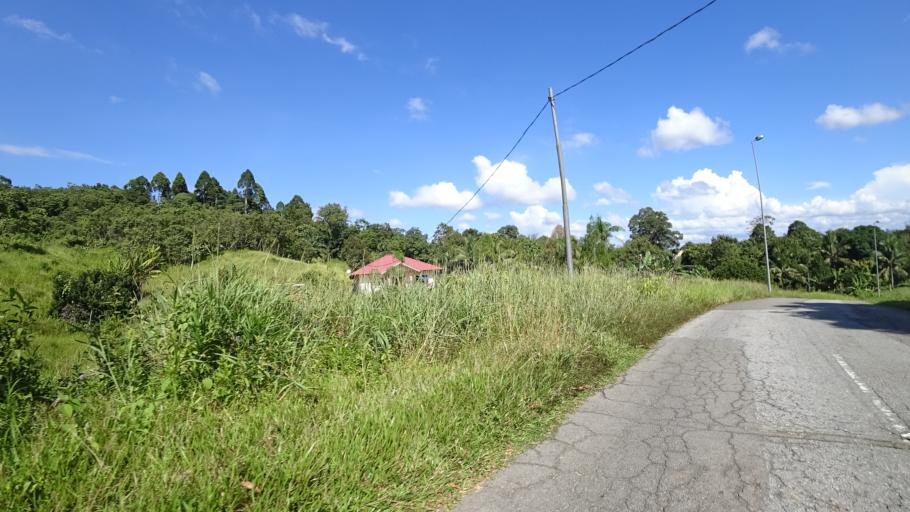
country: BN
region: Tutong
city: Tutong
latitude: 4.7448
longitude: 114.7869
